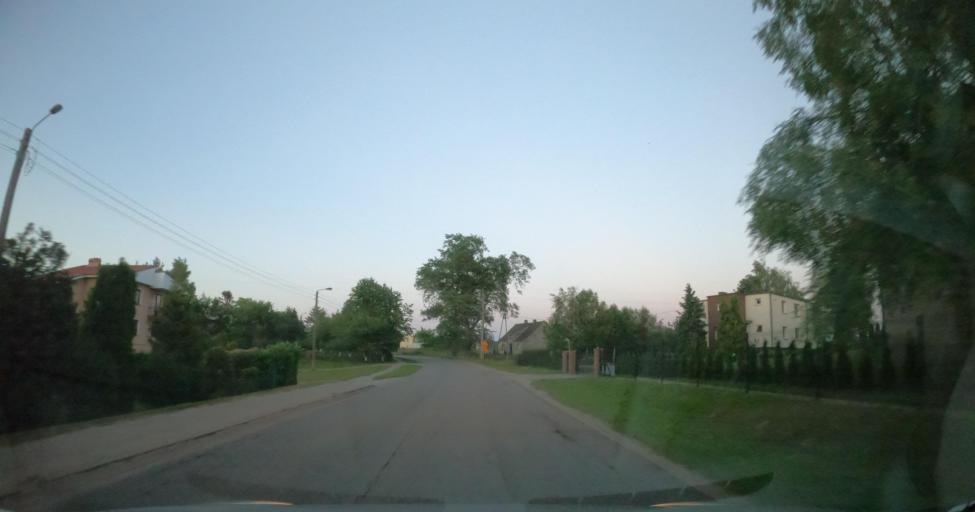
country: PL
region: Pomeranian Voivodeship
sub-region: Powiat wejherowski
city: Szemud
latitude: 54.4774
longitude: 18.1863
